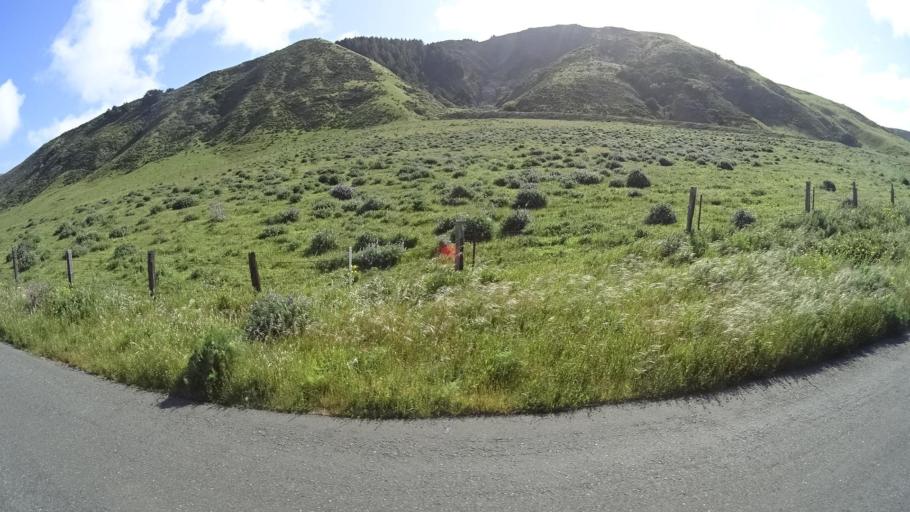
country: US
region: California
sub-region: Humboldt County
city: Ferndale
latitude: 40.4190
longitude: -124.3987
